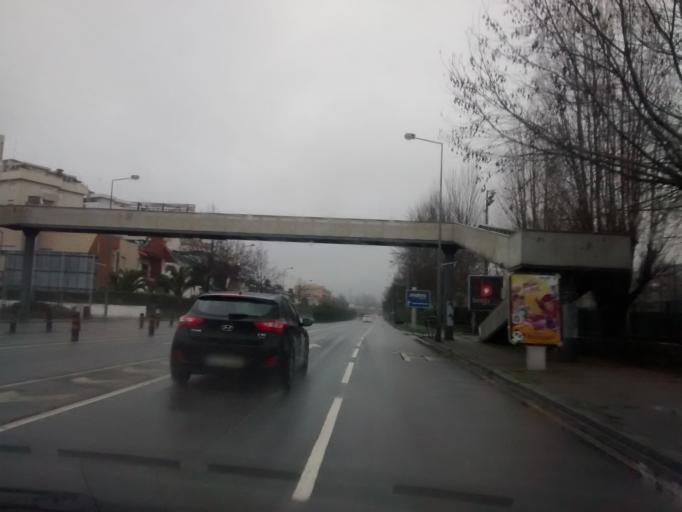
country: PT
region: Braga
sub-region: Braga
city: Braga
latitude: 41.5532
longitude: -8.4052
